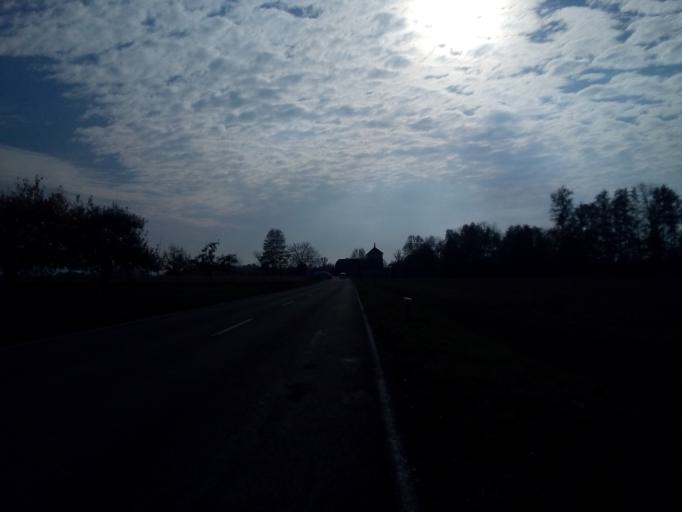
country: DE
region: Baden-Wuerttemberg
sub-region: Karlsruhe Region
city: Zell
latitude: 48.7001
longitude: 8.0677
